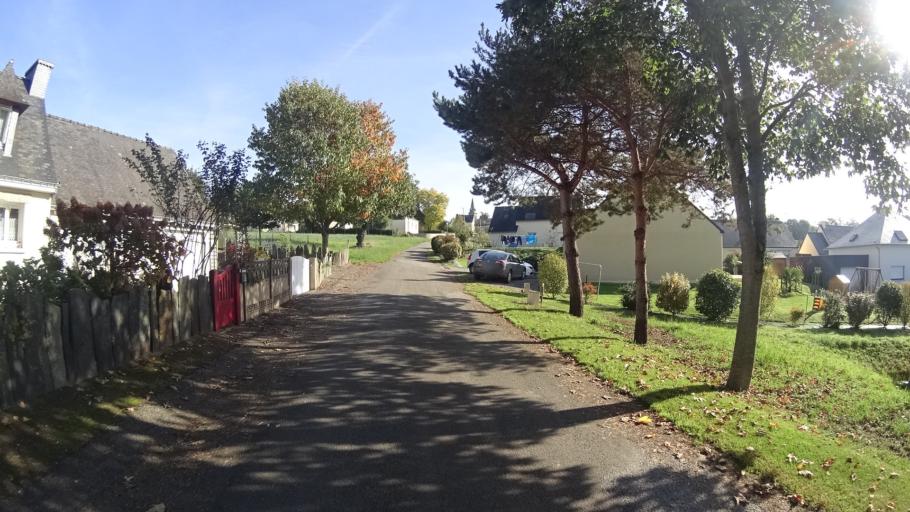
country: FR
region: Brittany
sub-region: Departement du Morbihan
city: Peillac
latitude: 47.7394
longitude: -2.2159
